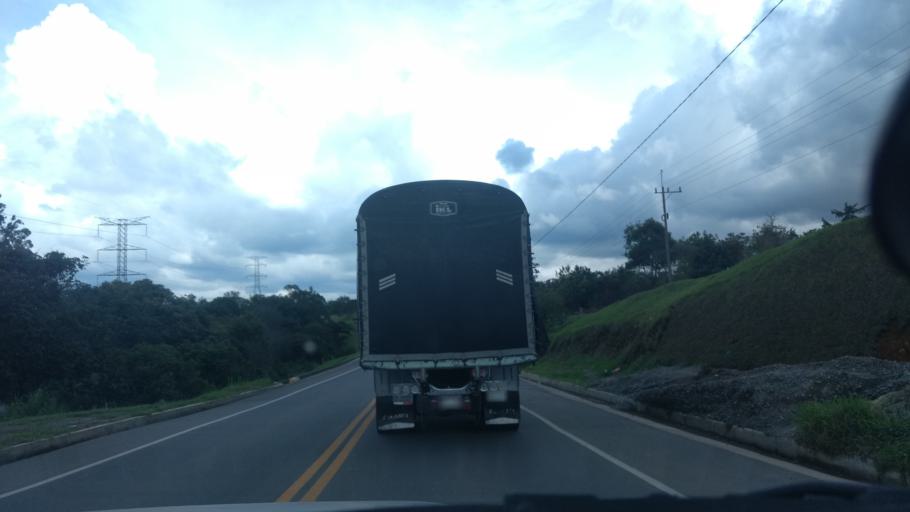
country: CO
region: Cauca
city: Popayan
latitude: 2.4958
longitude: -76.5644
